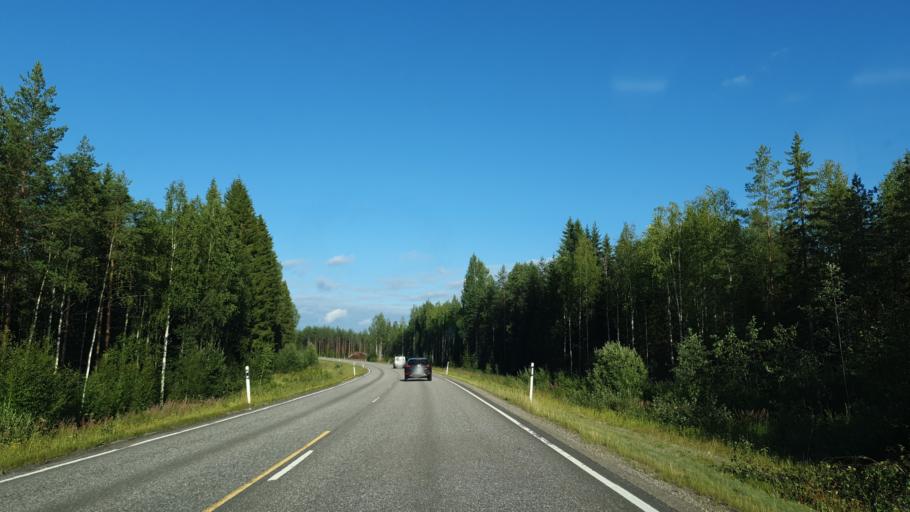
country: FI
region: North Karelia
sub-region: Joensuu
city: Outokumpu
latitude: 62.5199
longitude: 29.0140
